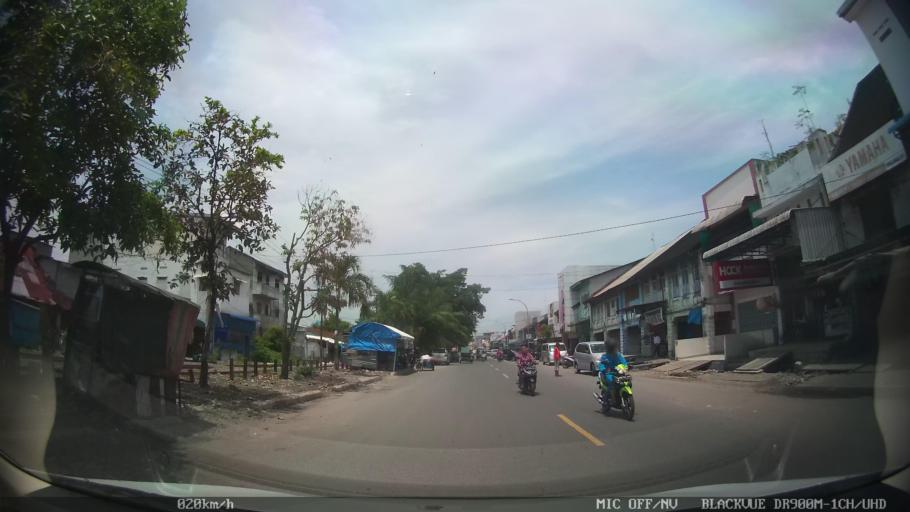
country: ID
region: North Sumatra
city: Belawan
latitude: 3.7827
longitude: 98.6861
